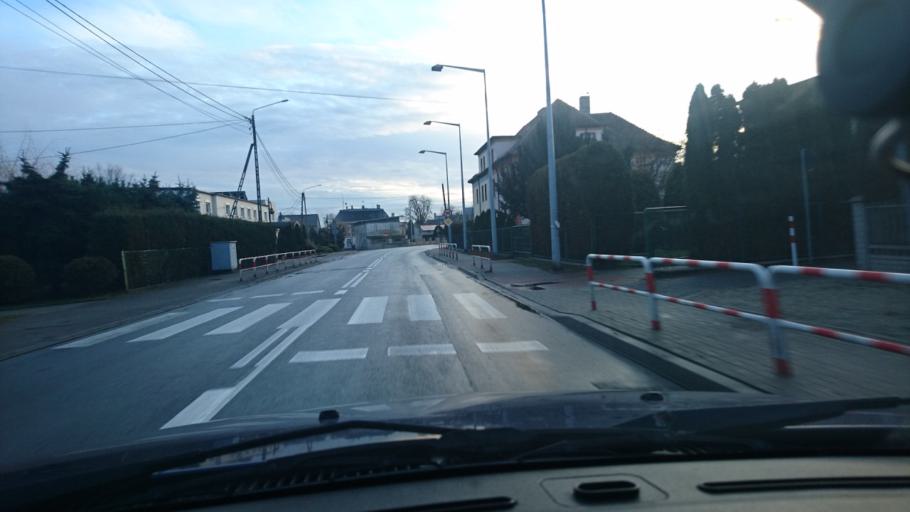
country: PL
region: Opole Voivodeship
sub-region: Powiat kluczborski
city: Byczyna
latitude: 51.1146
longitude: 18.2095
